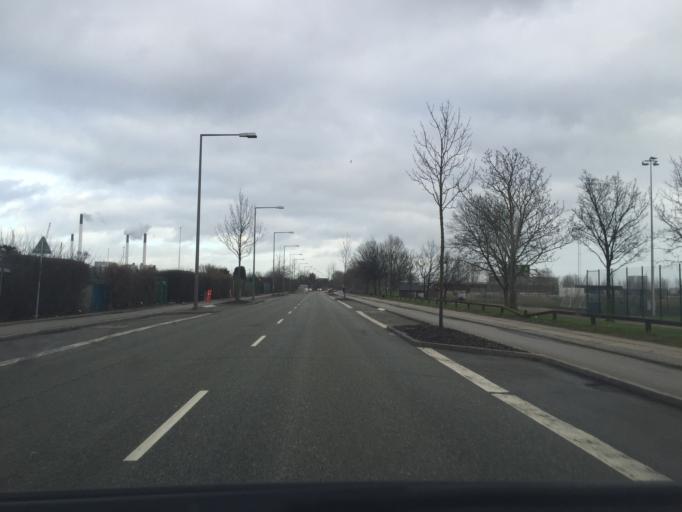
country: DK
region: Capital Region
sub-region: Kobenhavn
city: Christianshavn
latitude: 55.6732
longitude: 12.6096
